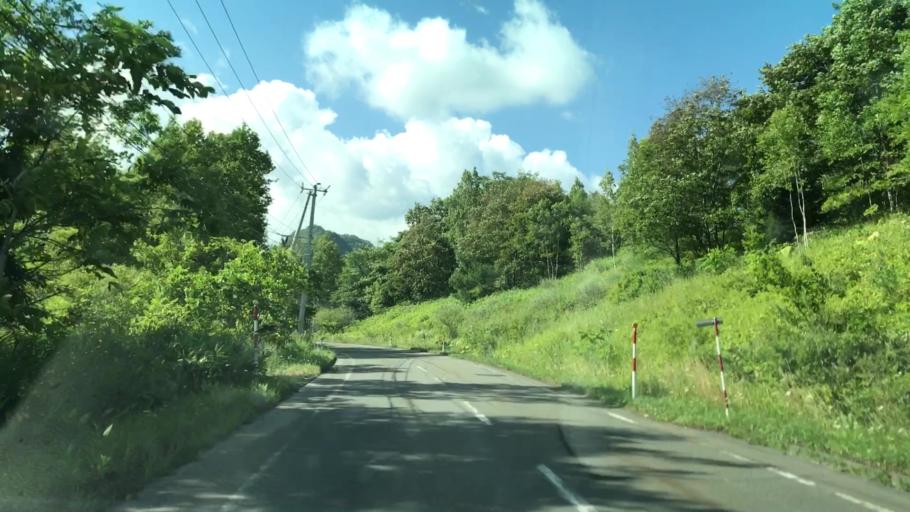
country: JP
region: Hokkaido
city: Shimo-furano
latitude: 42.8494
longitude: 142.4214
